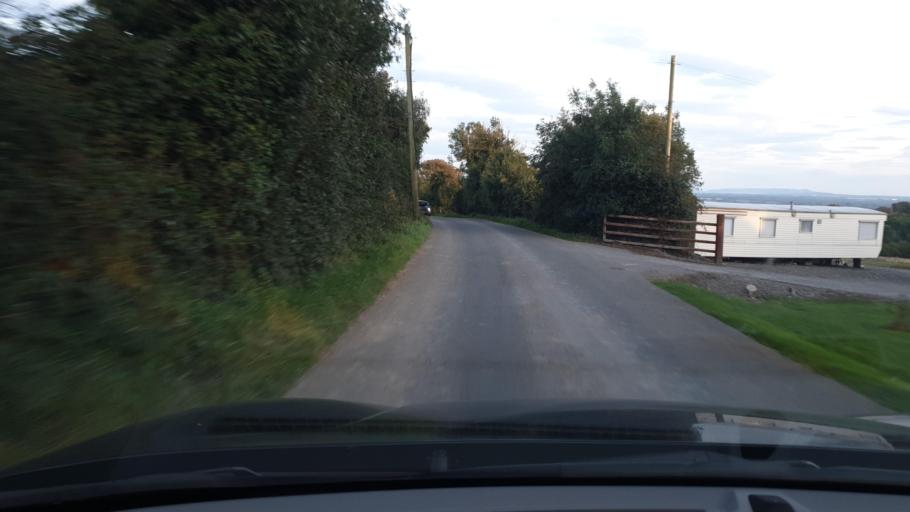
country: IE
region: Leinster
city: Balrothery
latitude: 53.5675
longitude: -6.2385
